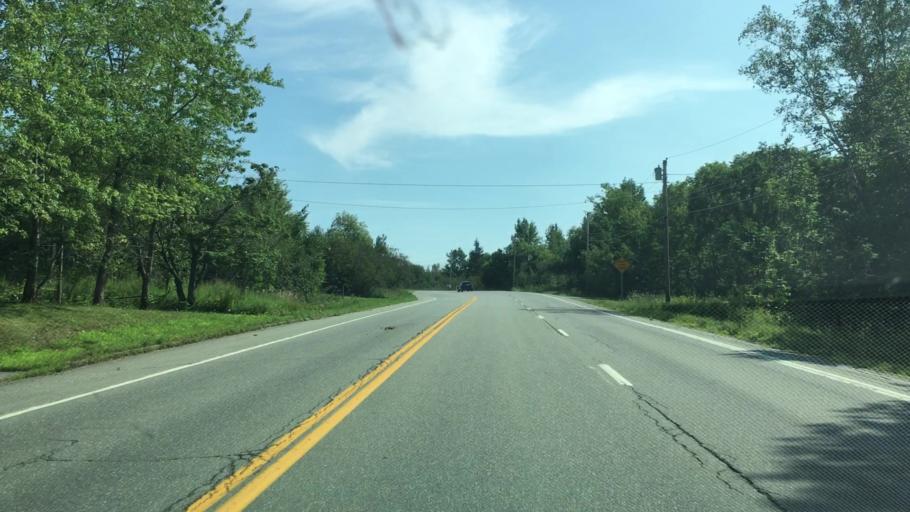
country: US
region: Maine
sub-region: Penobscot County
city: Orrington
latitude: 44.6908
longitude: -68.8478
